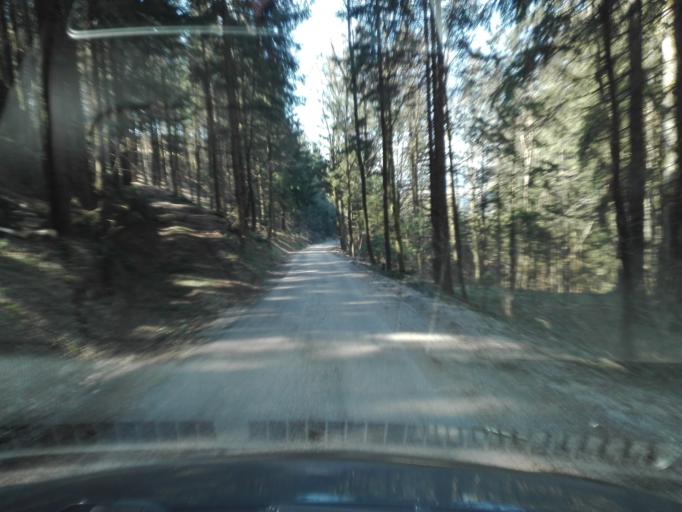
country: AT
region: Upper Austria
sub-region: Politischer Bezirk Perg
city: Bad Kreuzen
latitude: 48.3721
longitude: 14.7608
